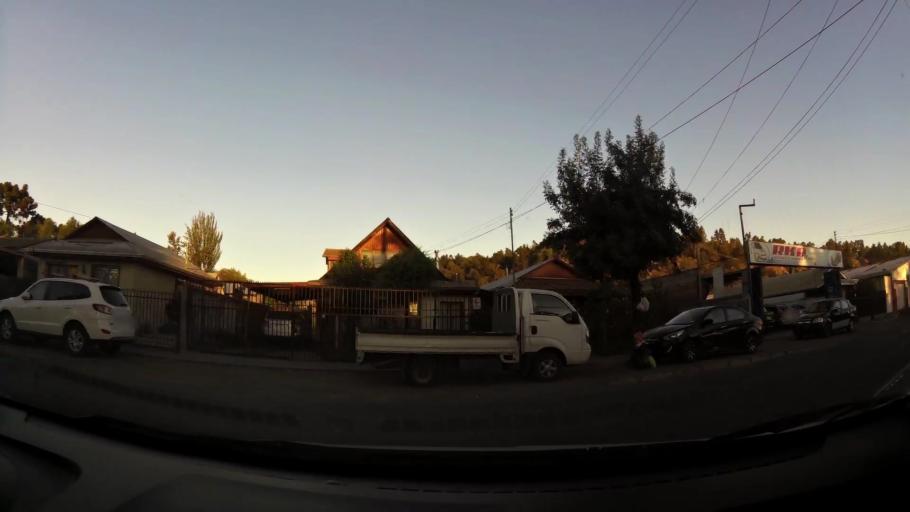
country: CL
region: Maule
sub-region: Provincia de Curico
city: Curico
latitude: -34.9776
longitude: -71.2353
